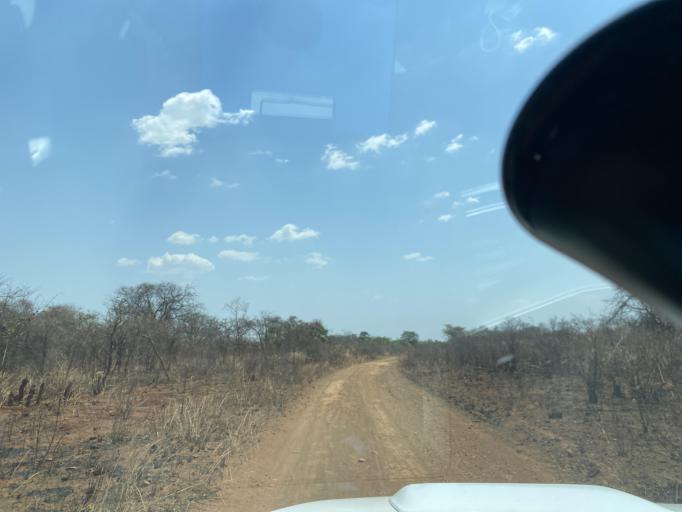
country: ZM
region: Lusaka
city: Lusaka
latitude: -15.5091
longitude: 27.9919
